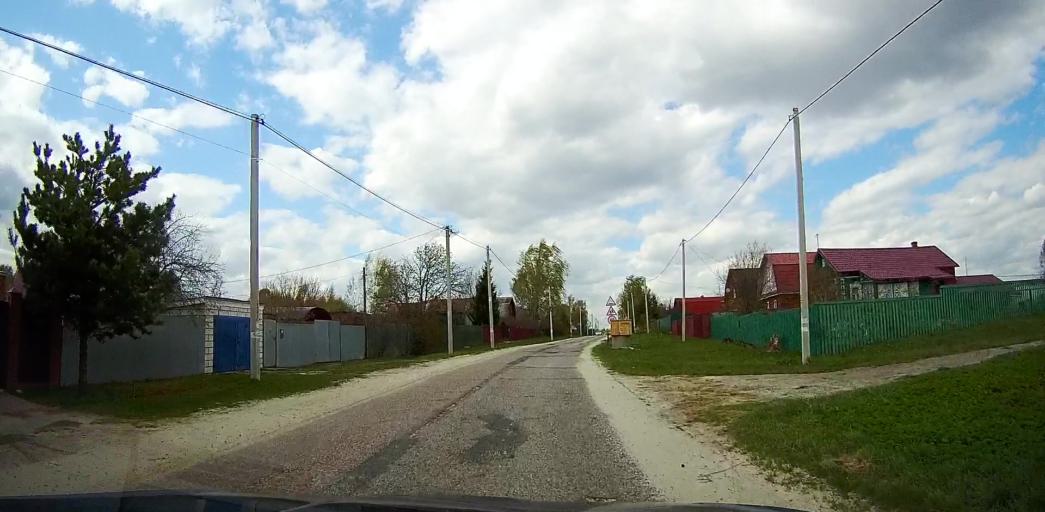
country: RU
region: Moskovskaya
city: Davydovo
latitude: 55.6361
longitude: 38.7817
